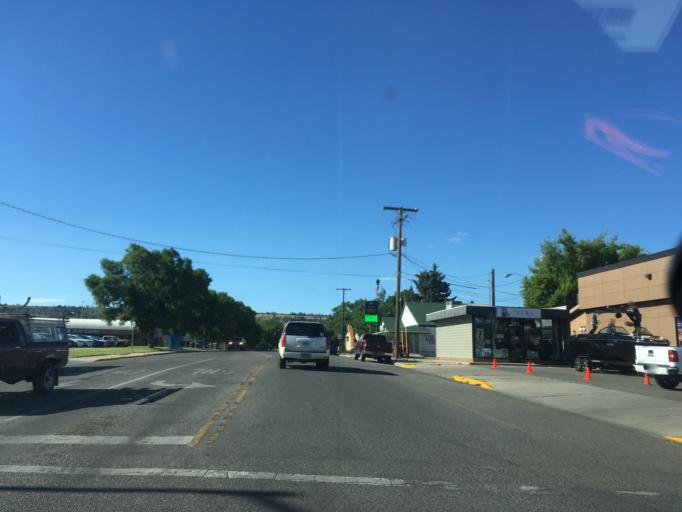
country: US
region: Montana
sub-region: Yellowstone County
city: Billings
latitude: 45.7841
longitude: -108.5538
